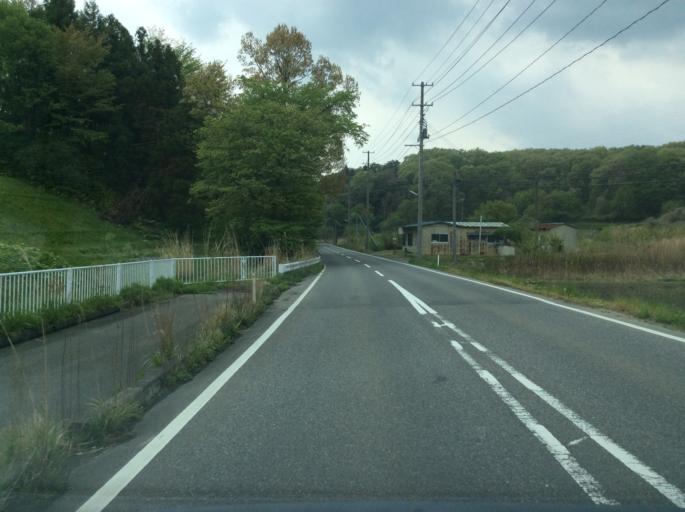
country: JP
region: Fukushima
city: Koriyama
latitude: 37.3903
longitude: 140.4287
